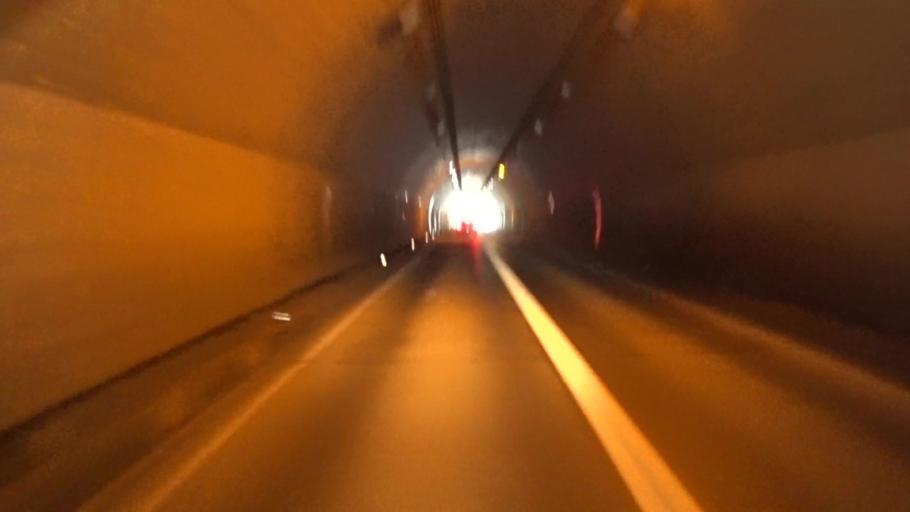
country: JP
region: Shiga Prefecture
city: Kitahama
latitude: 35.2105
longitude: 135.8564
